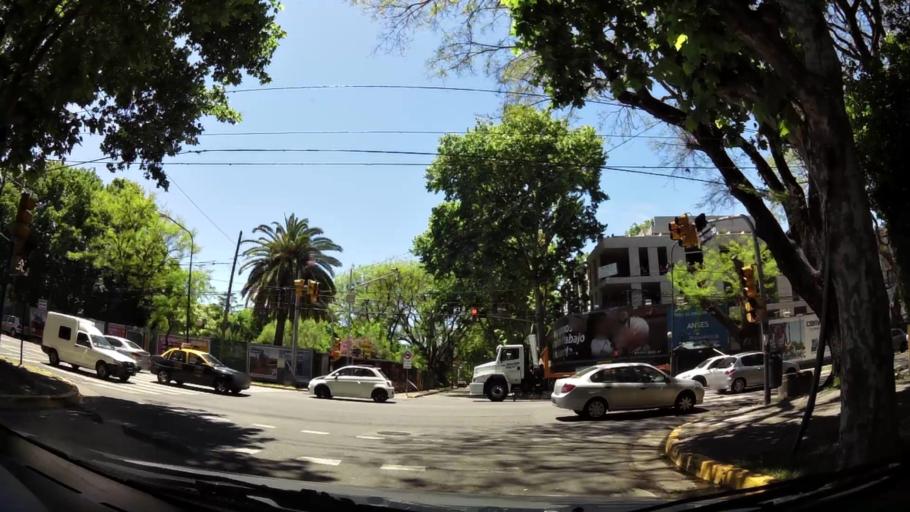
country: AR
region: Buenos Aires
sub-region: Partido de Vicente Lopez
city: Olivos
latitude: -34.4871
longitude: -58.4860
